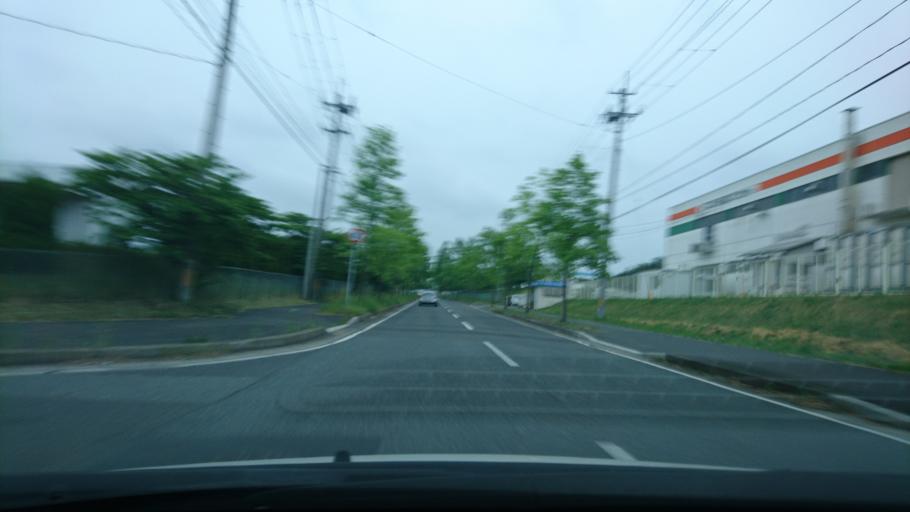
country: JP
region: Iwate
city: Ichinoseki
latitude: 38.9192
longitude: 141.1560
